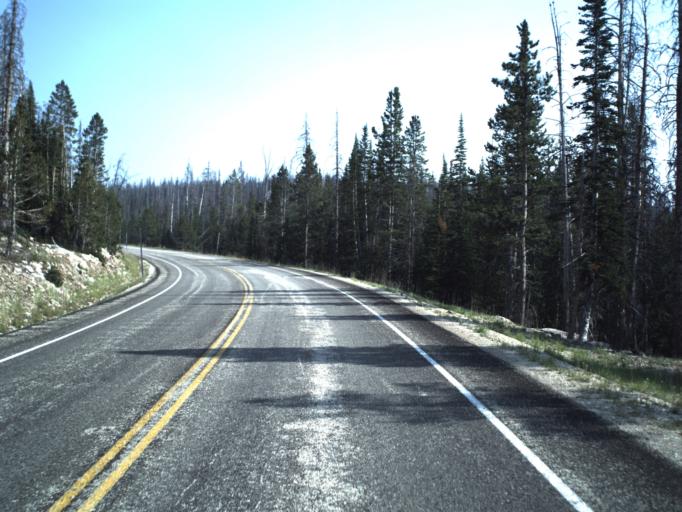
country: US
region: Utah
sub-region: Summit County
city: Kamas
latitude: 40.6820
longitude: -110.9271
